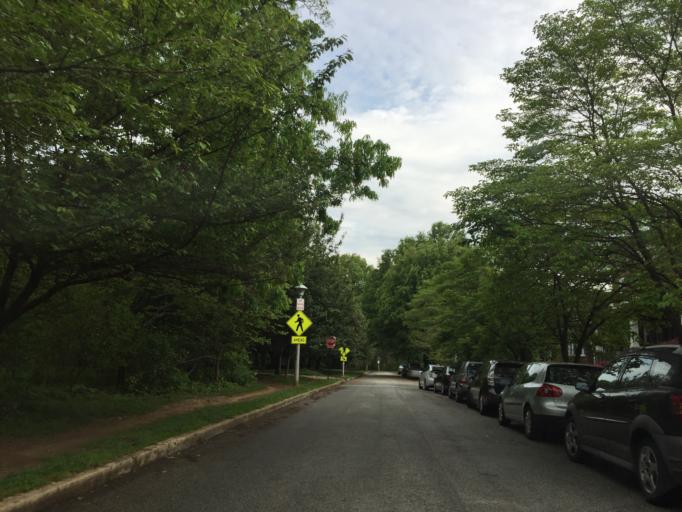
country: US
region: Maryland
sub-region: City of Baltimore
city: Baltimore
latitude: 39.3343
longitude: -76.6258
